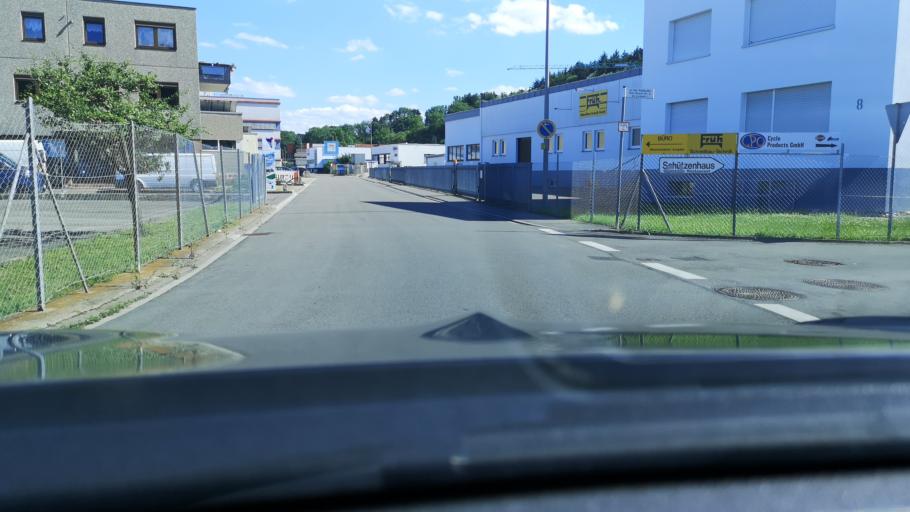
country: DE
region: Baden-Wuerttemberg
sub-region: Regierungsbezirk Stuttgart
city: Neckartenzlingen
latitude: 48.5845
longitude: 9.2279
